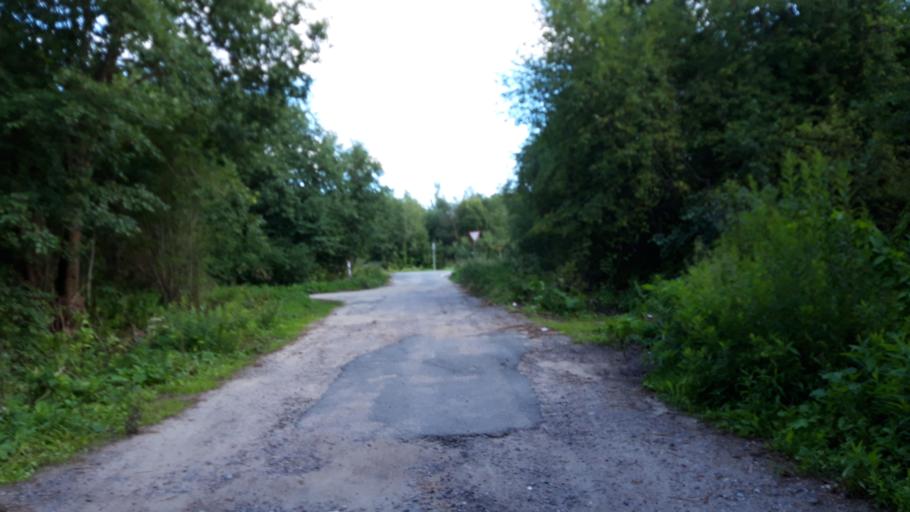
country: RU
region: Tverskaya
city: Konakovo
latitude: 56.6719
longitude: 36.7308
